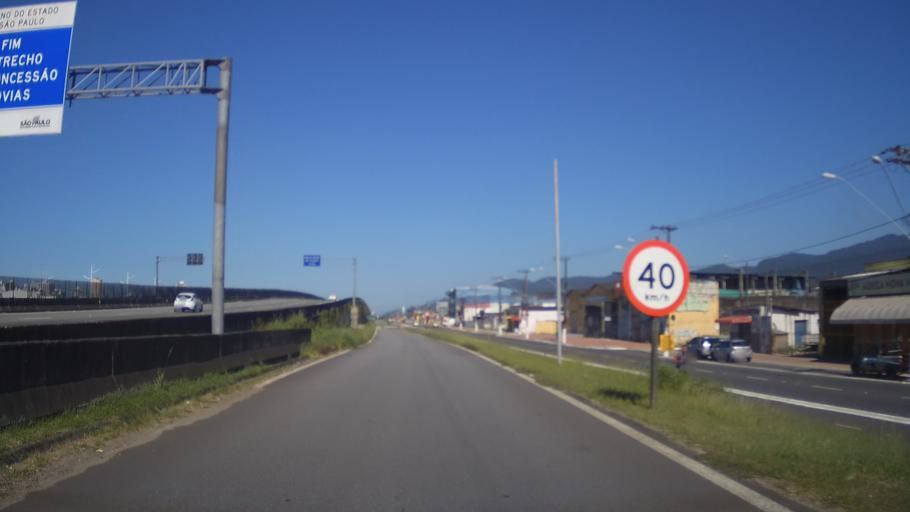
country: BR
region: Sao Paulo
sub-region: Mongagua
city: Mongagua
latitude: -24.0372
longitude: -46.5172
